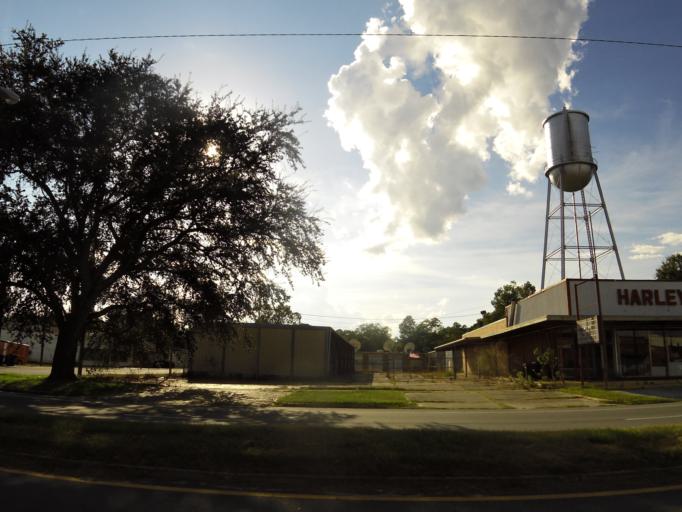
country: US
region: Georgia
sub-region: Brooks County
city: Quitman
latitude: 30.7836
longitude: -83.5601
